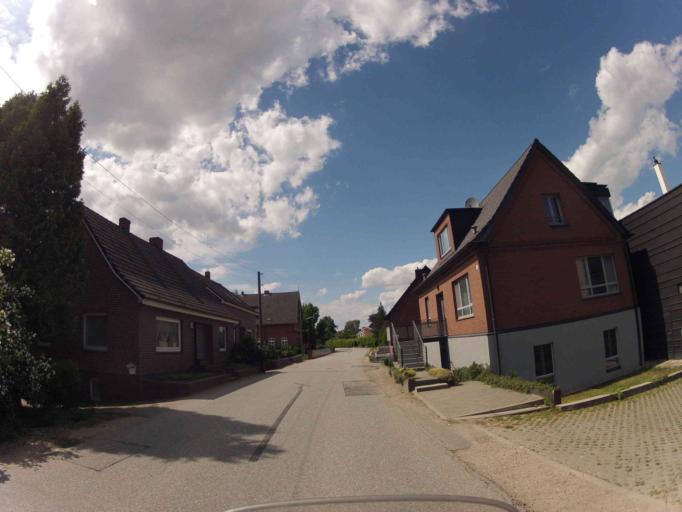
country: DE
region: Hamburg
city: Bergedorf
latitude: 53.4429
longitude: 10.1813
